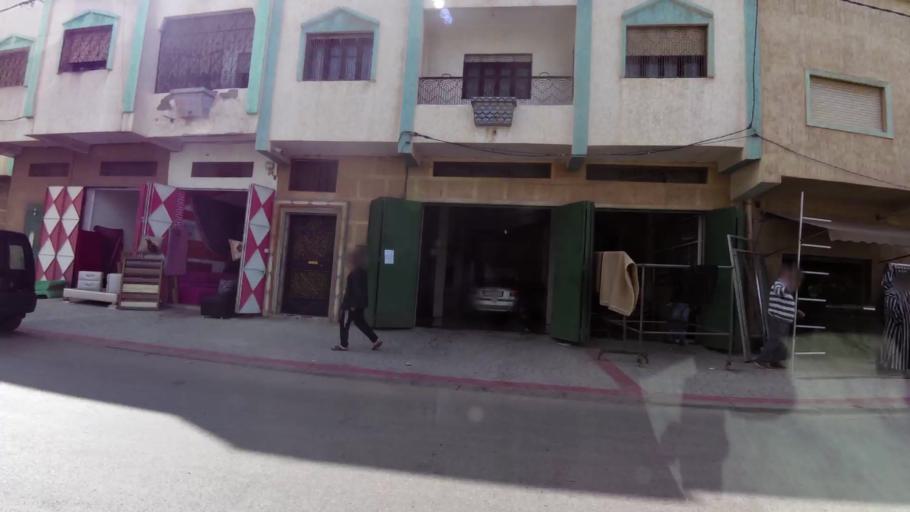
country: MA
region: Tanger-Tetouan
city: Tetouan
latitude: 35.5860
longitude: -5.3565
